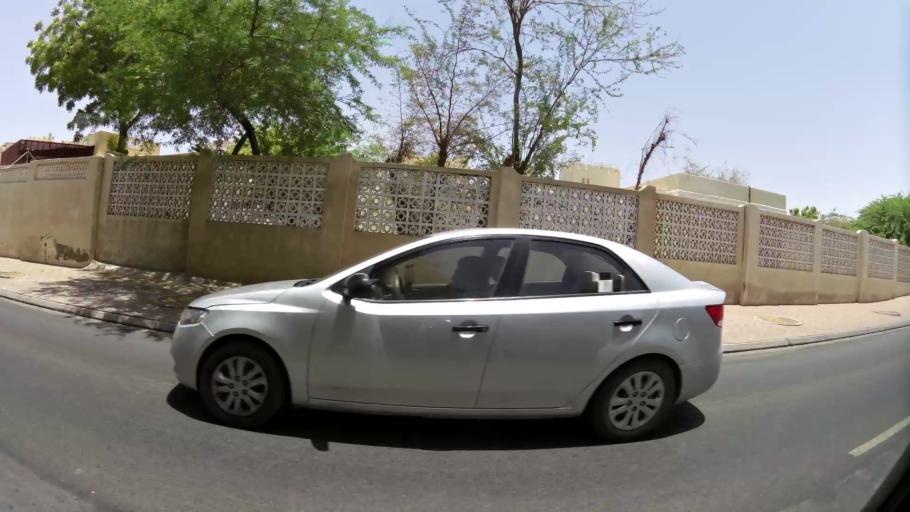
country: OM
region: Muhafazat Masqat
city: Bawshar
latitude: 23.5984
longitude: 58.4495
